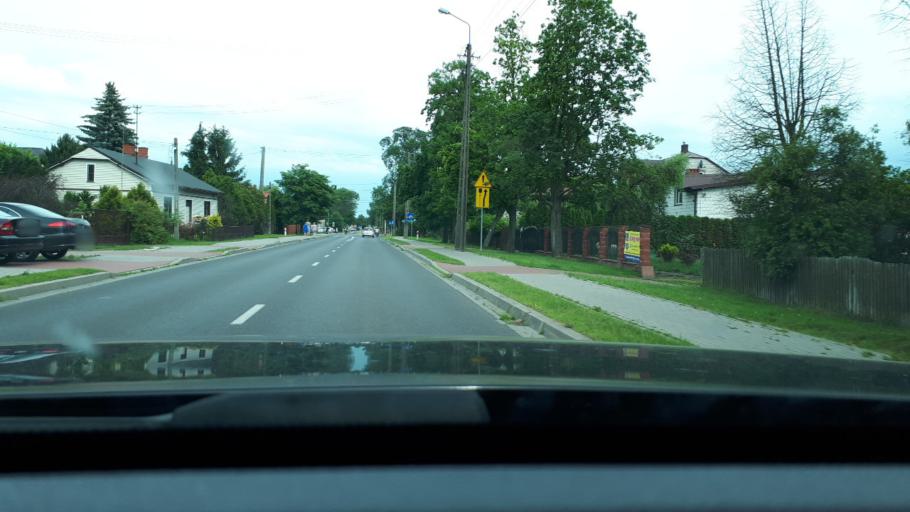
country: PL
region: Masovian Voivodeship
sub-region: Powiat warszawski zachodni
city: Kampinos
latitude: 52.2686
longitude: 20.4562
